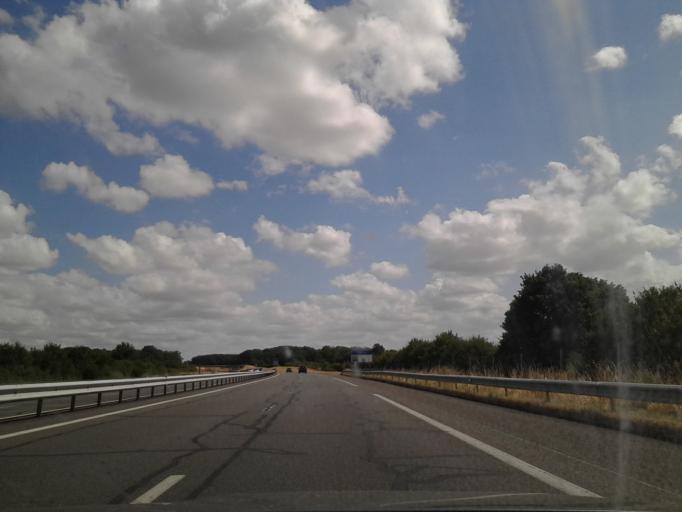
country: FR
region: Centre
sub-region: Departement du Cher
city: Orval
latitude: 46.7687
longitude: 2.4056
